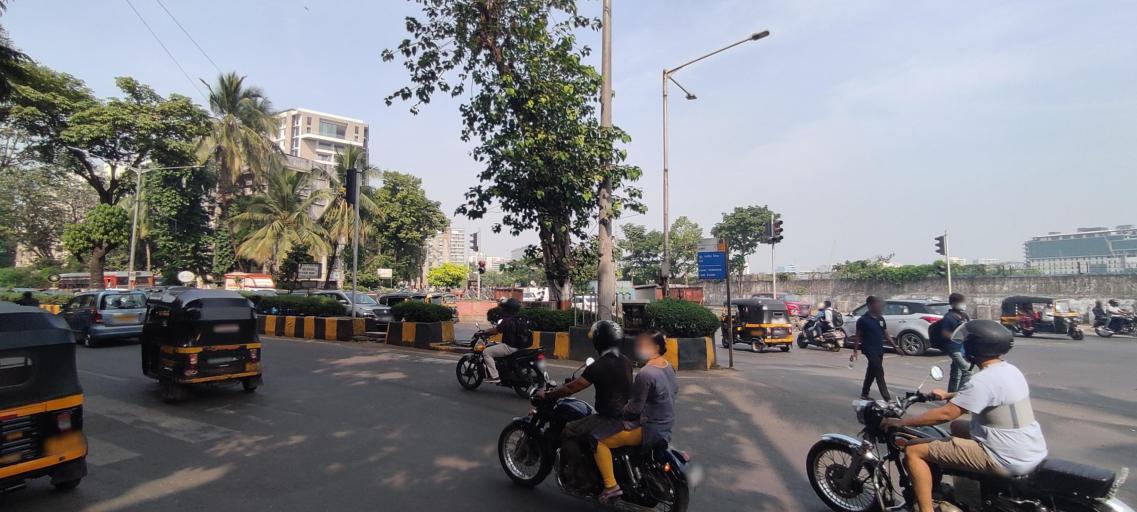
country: IN
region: Maharashtra
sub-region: Mumbai Suburban
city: Mumbai
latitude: 19.1172
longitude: 72.8296
